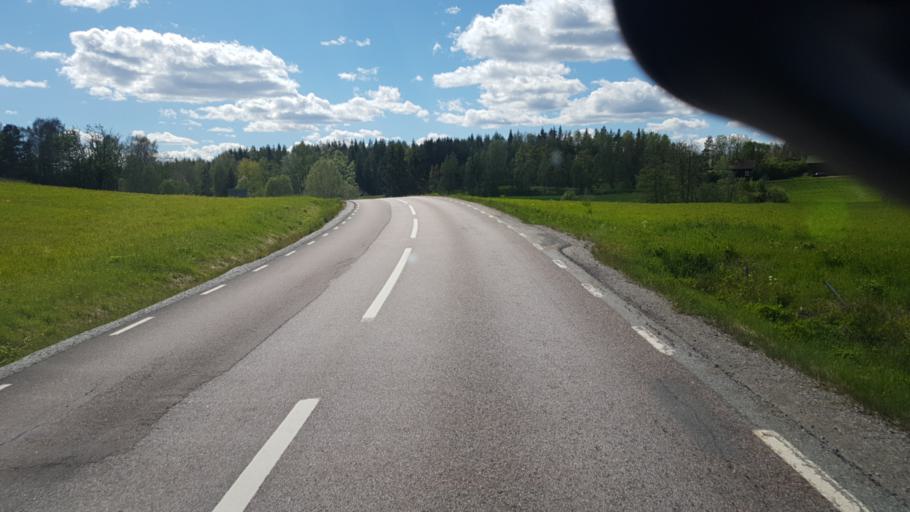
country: SE
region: Vaermland
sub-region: Sunne Kommun
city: Sunne
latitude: 59.6572
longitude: 12.9488
